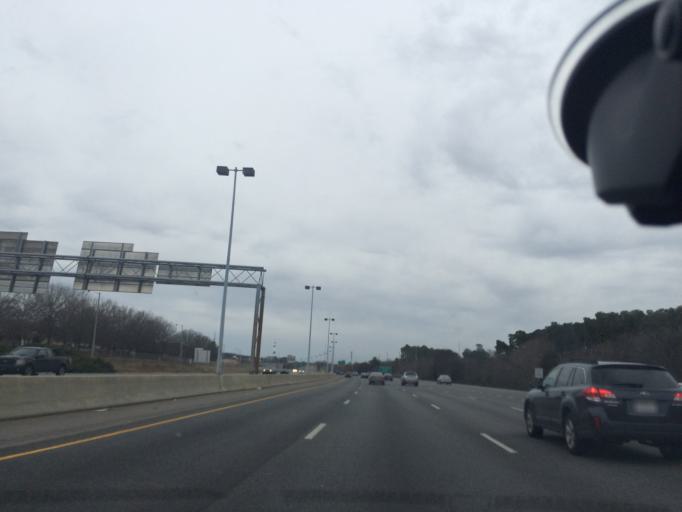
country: US
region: Alabama
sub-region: Madison County
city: Redstone Arsenal
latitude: 34.7189
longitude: -86.6318
